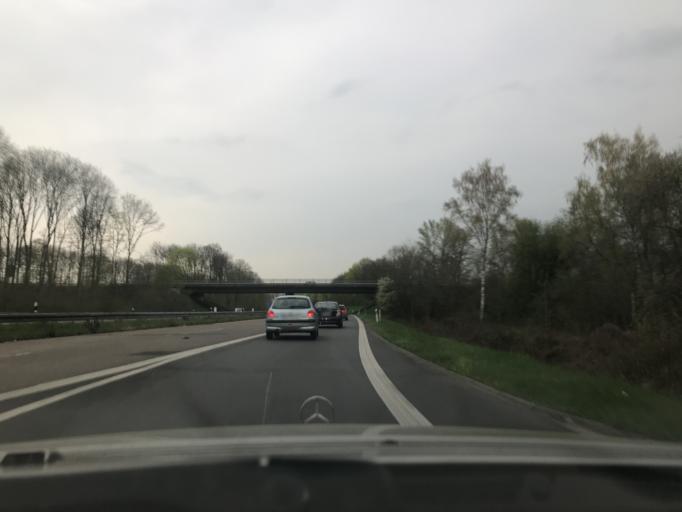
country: DE
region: North Rhine-Westphalia
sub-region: Regierungsbezirk Dusseldorf
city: Korschenbroich
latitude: 51.2207
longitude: 6.4921
